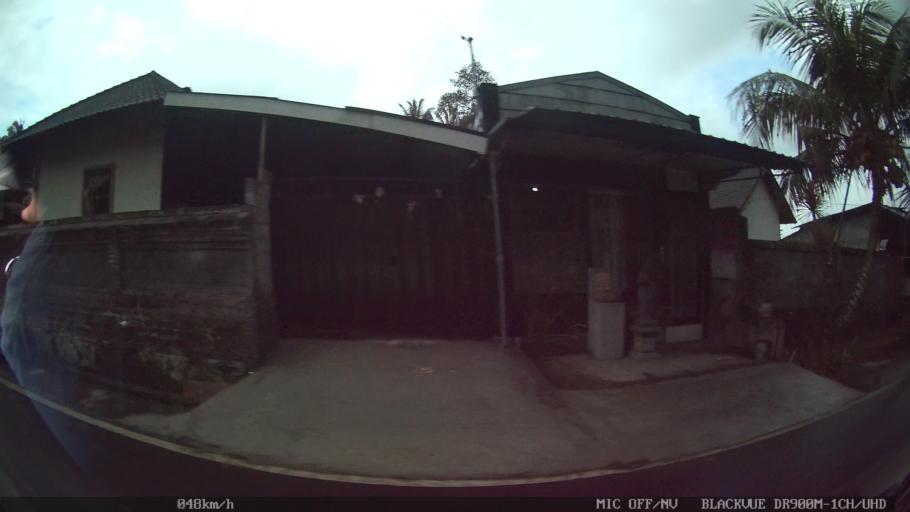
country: ID
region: Bali
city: Banjar Teguan
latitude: -8.5107
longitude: 115.2294
